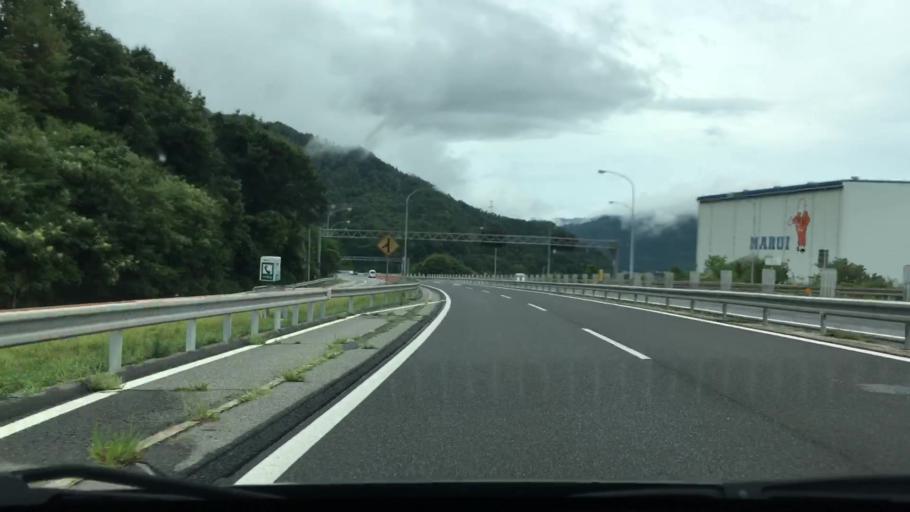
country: JP
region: Hiroshima
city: Hiroshima-shi
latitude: 34.5727
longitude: 132.4565
